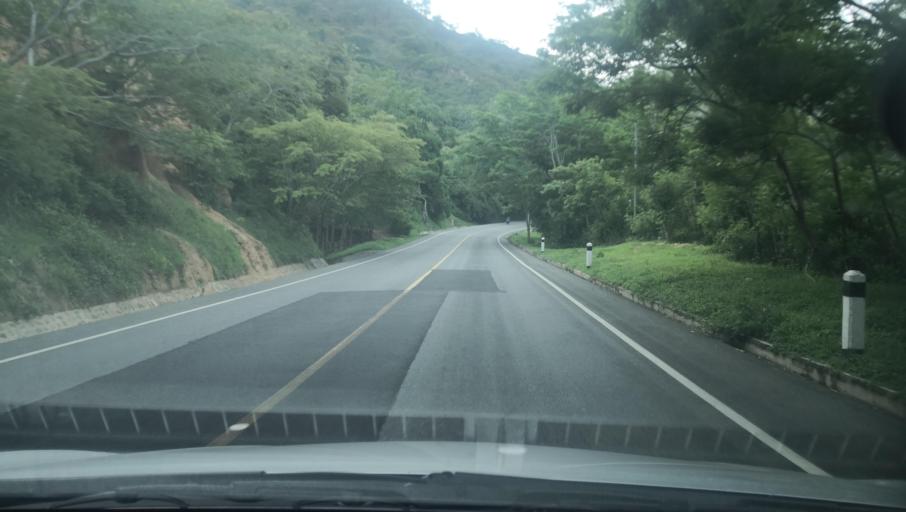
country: NI
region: Nueva Segovia
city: Mozonte
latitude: 13.6914
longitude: -86.4877
